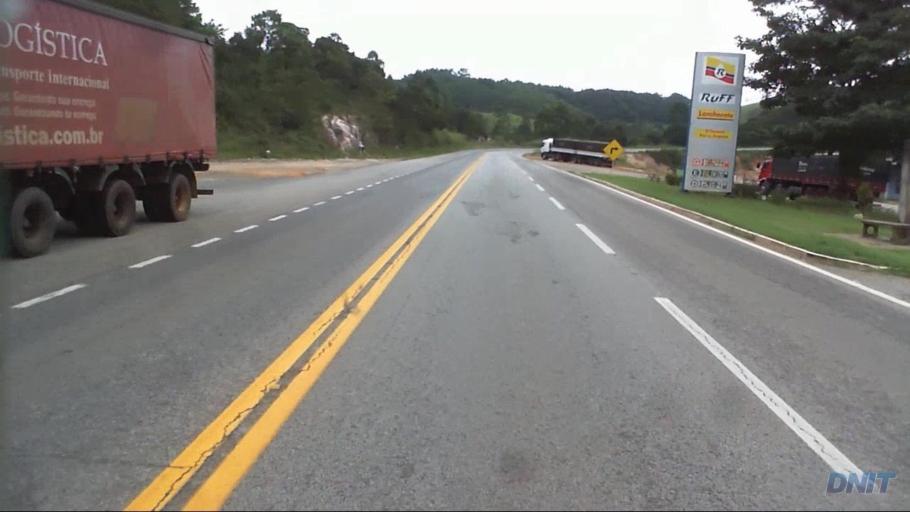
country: BR
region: Minas Gerais
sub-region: Caete
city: Caete
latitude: -19.7537
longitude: -43.5285
